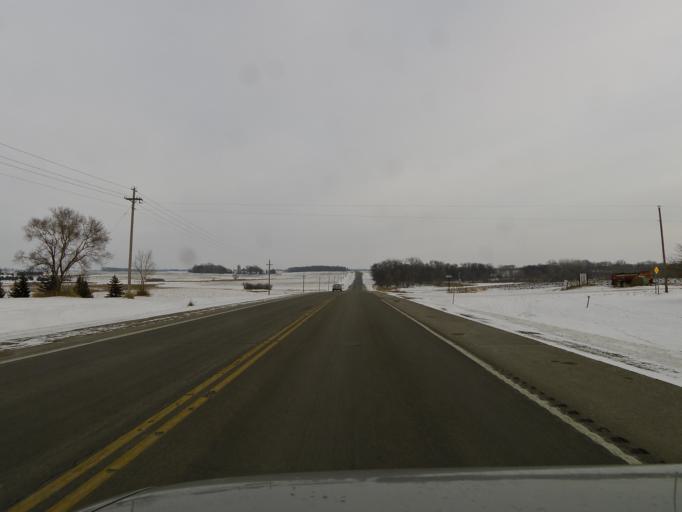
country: US
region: Minnesota
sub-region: McLeod County
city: Lester Prairie
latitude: 44.9063
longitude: -94.0234
